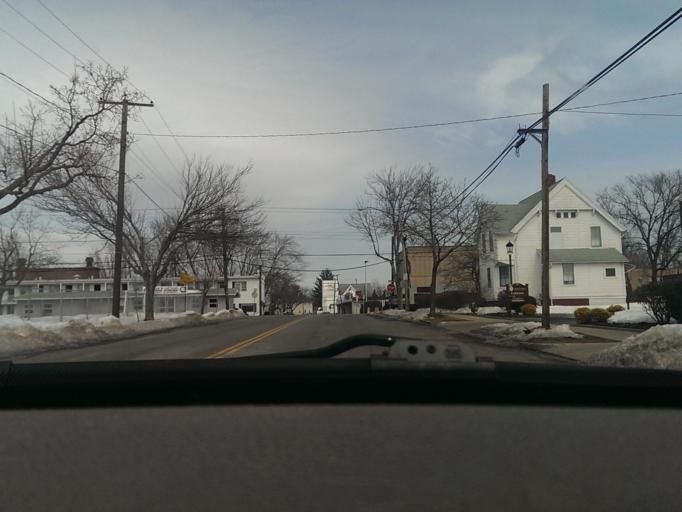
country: US
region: Massachusetts
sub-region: Hampden County
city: Ludlow
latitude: 42.1579
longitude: -72.4808
